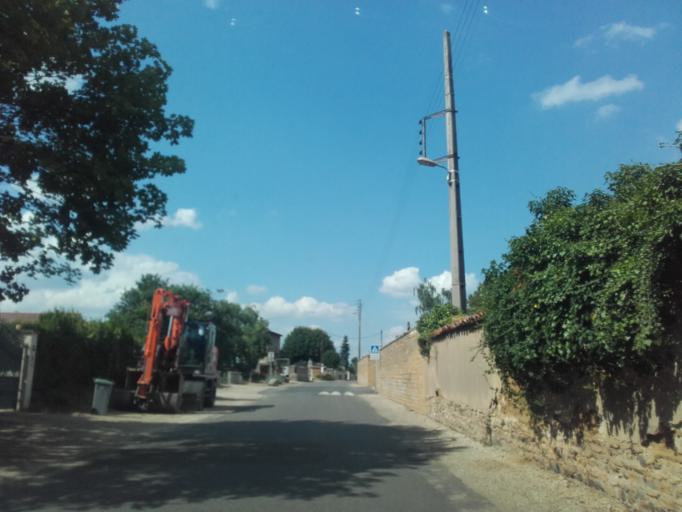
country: FR
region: Bourgogne
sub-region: Departement de Saone-et-Loire
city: La Chapelle-de-Guinchay
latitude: 46.2009
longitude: 4.7701
